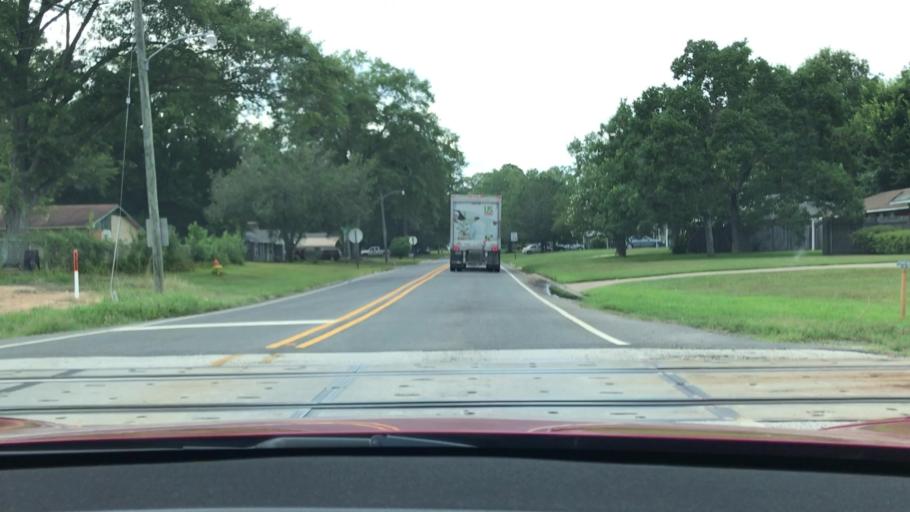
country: US
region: Louisiana
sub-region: De Soto Parish
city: Stonewall
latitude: 32.3949
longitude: -93.7998
